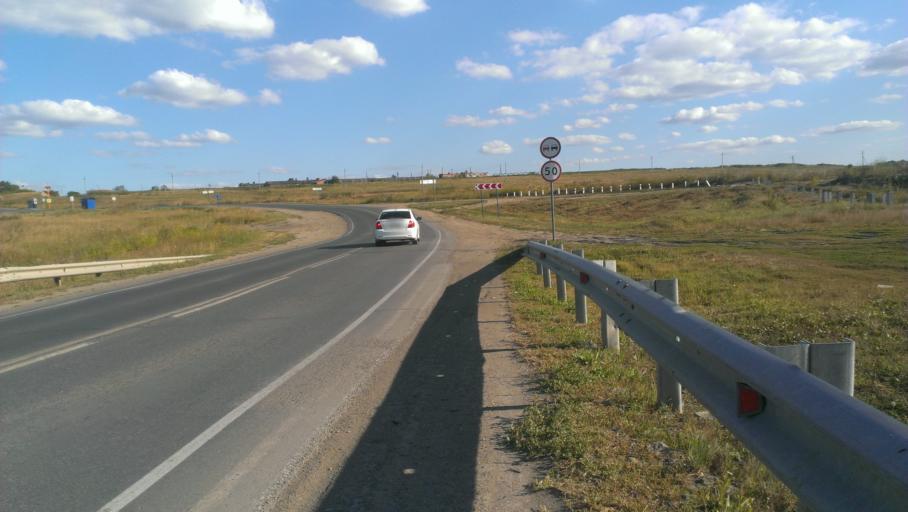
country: RU
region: Altai Krai
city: Gon'ba
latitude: 53.4148
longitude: 83.5505
